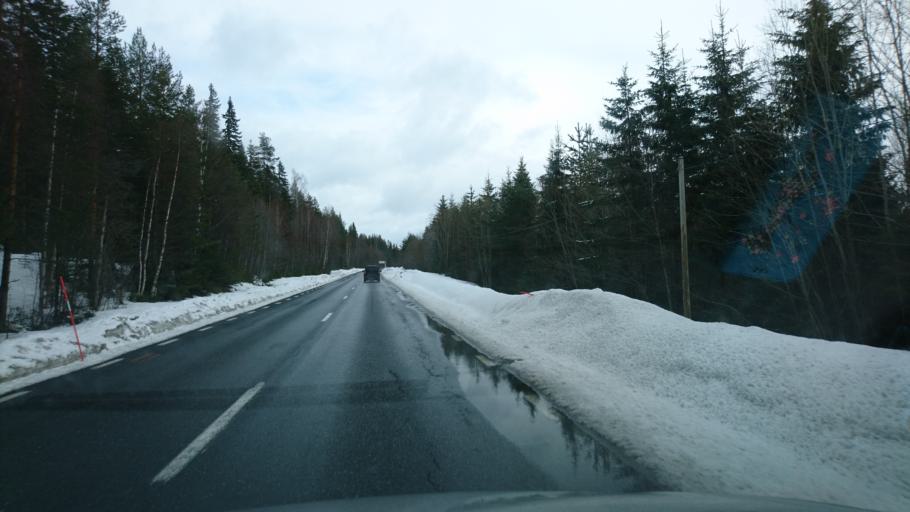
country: SE
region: Vaesternorrland
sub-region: Solleftea Kommun
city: Solleftea
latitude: 63.0471
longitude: 17.0611
